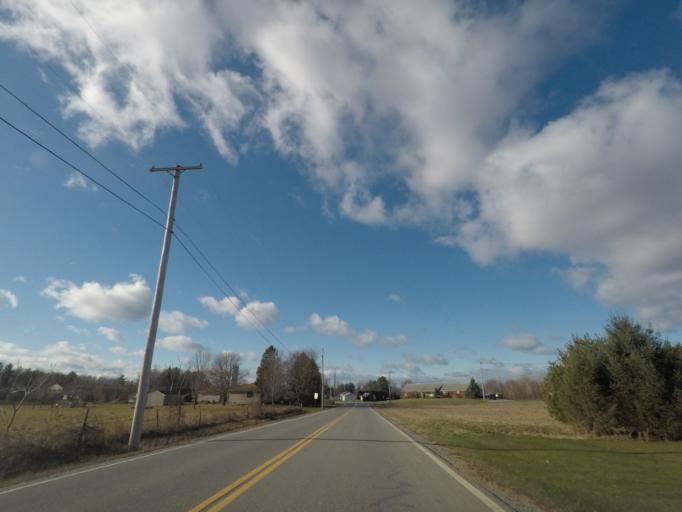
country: US
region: New York
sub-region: Saratoga County
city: Waterford
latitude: 42.8333
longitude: -73.6995
